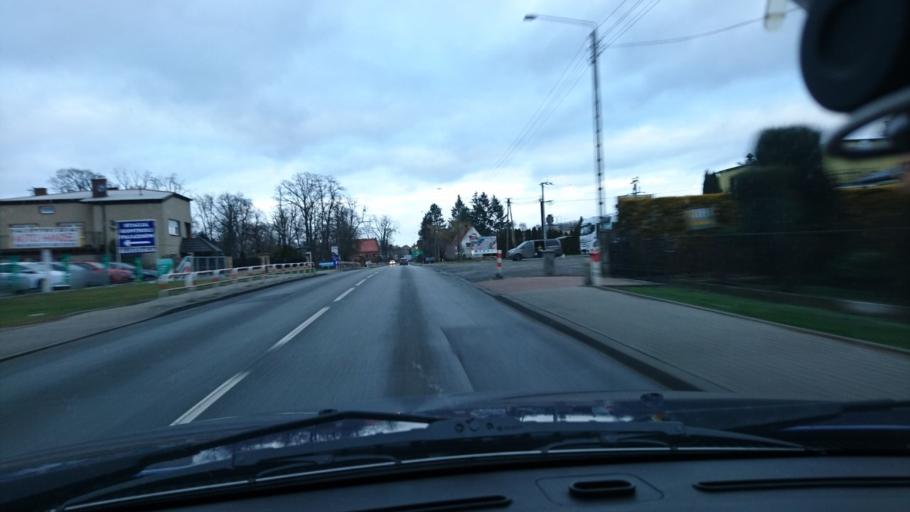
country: PL
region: Opole Voivodeship
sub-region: Powiat kluczborski
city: Byczyna
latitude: 51.1102
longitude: 18.2075
